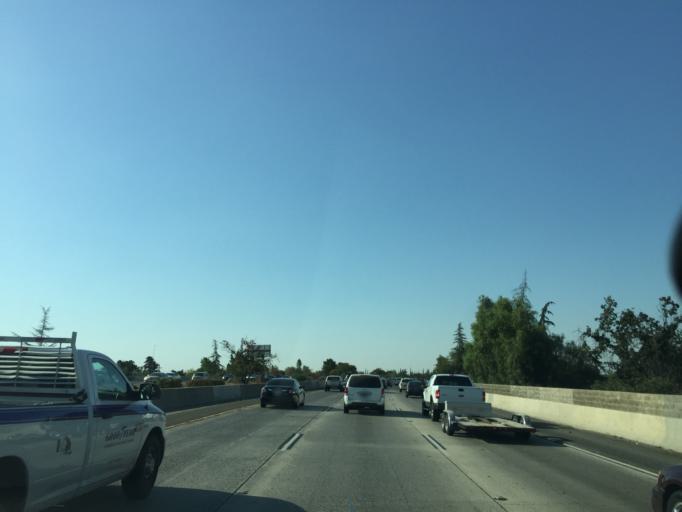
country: US
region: California
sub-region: Fresno County
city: Fresno
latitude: 36.7713
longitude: -119.7843
